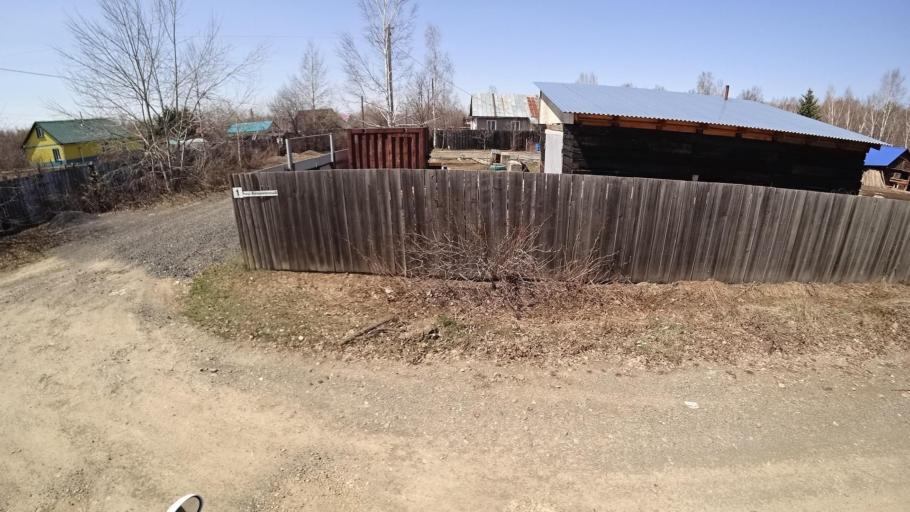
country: RU
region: Khabarovsk Krai
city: Khurba
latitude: 50.4147
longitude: 136.8621
